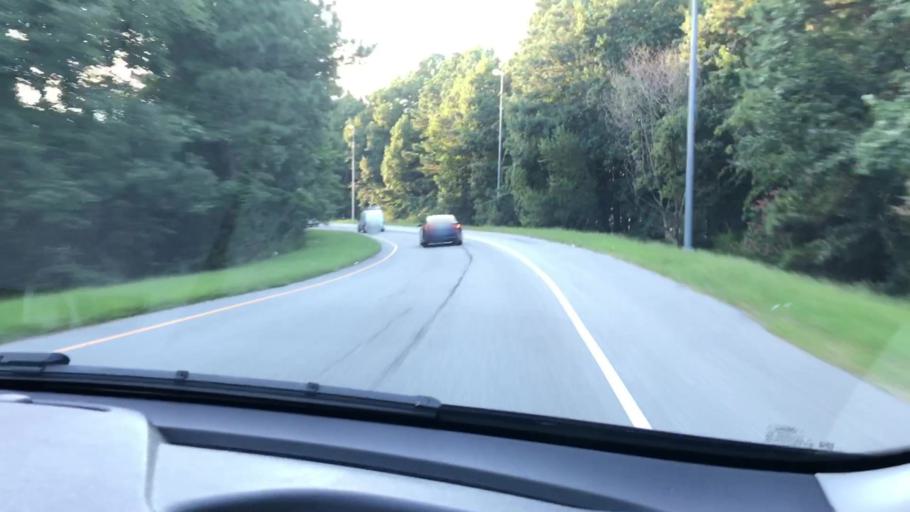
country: US
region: Virginia
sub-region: City of Hampton
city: Hampton
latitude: 37.0605
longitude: -76.4153
